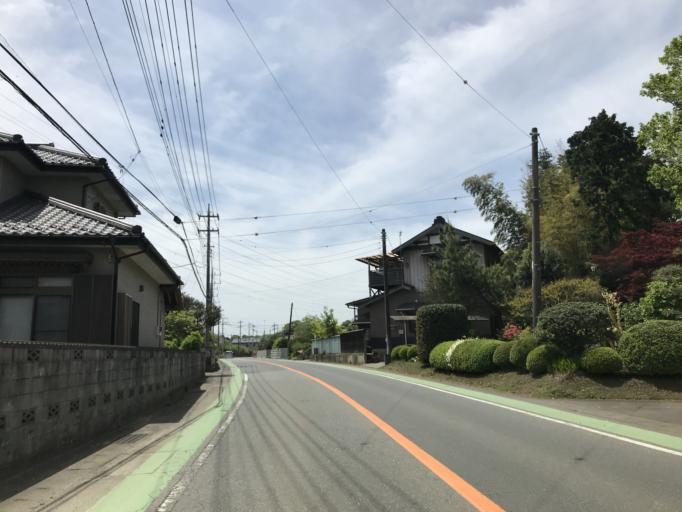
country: JP
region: Ibaraki
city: Mitsukaido
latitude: 35.9893
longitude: 139.9557
